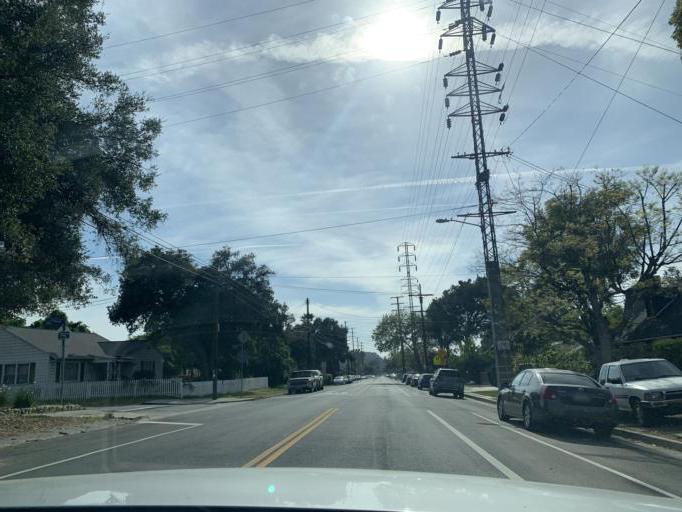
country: US
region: California
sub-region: Los Angeles County
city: South Pasadena
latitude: 34.1199
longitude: -118.1703
